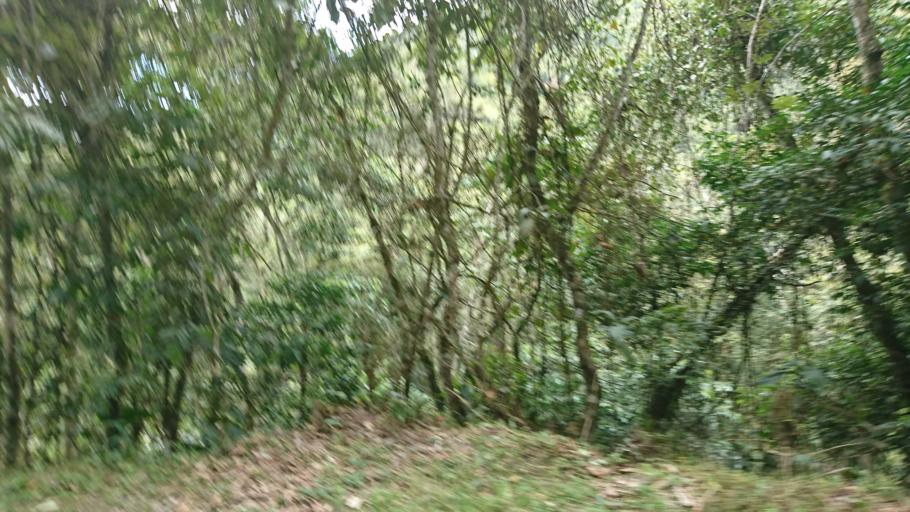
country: BO
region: La Paz
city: Coroico
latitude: -16.1133
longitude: -67.7889
